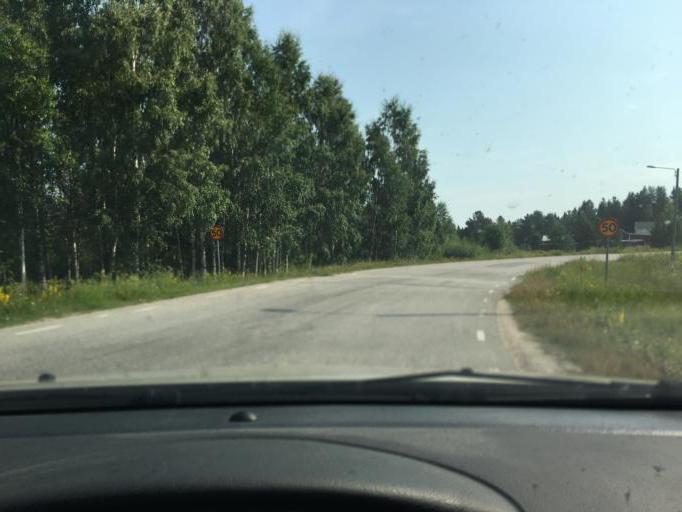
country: SE
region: Norrbotten
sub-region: Kalix Kommun
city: Kalix
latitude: 65.7833
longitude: 23.1725
